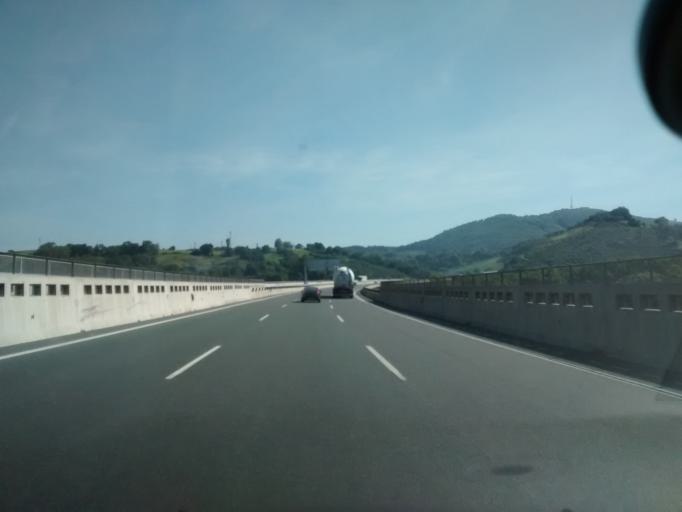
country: ES
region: Basque Country
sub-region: Provincia de Guipuzcoa
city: Astigarraga
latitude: 43.2853
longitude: -1.9556
